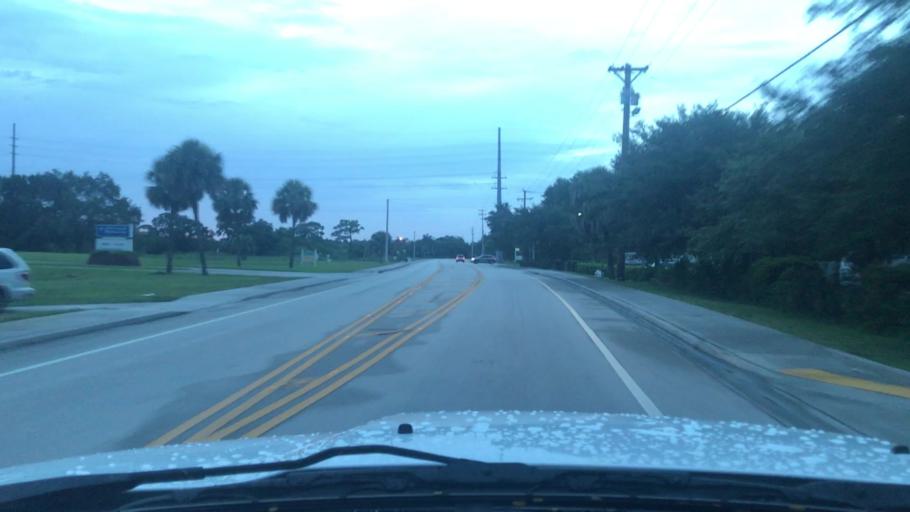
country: US
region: Florida
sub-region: Indian River County
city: Florida Ridge
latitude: 27.6022
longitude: -80.3861
